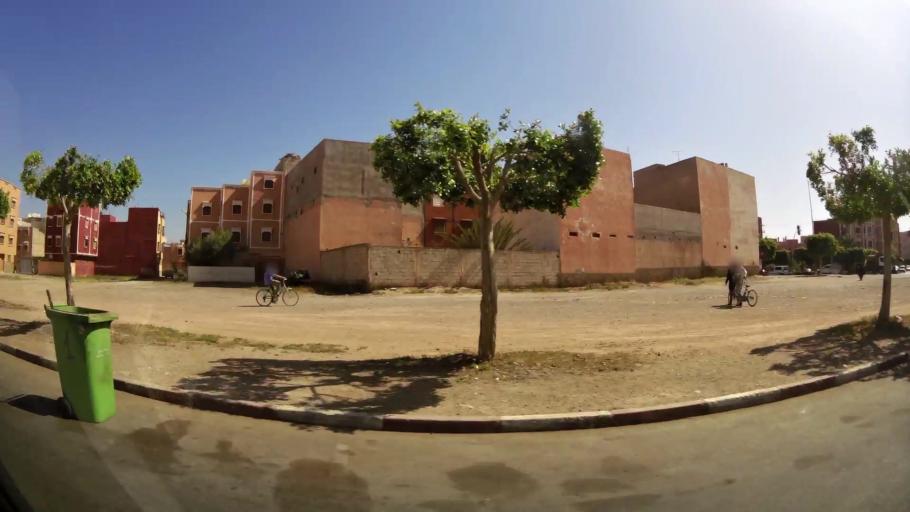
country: MA
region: Souss-Massa-Draa
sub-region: Inezgane-Ait Mellou
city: Inezgane
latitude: 30.3383
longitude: -9.5047
